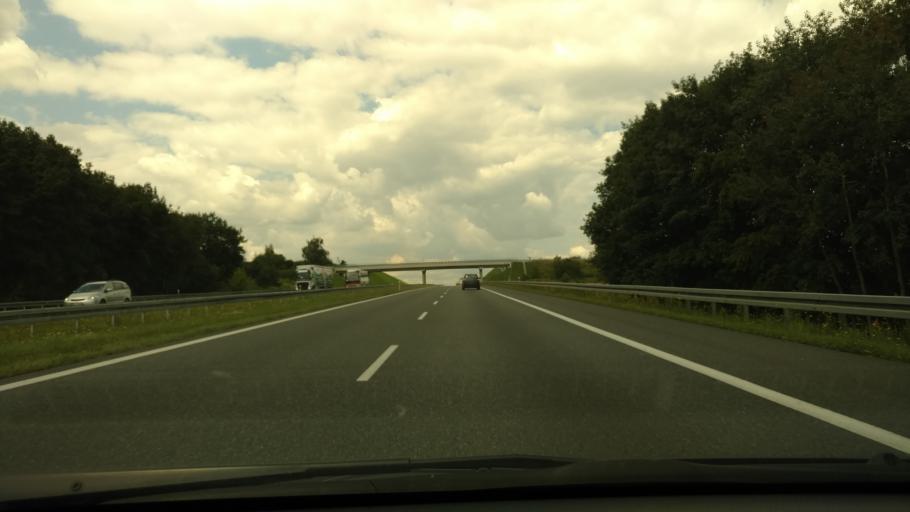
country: PL
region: Silesian Voivodeship
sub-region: Powiat bierunsko-ledzinski
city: Imielin
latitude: 50.1616
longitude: 19.2258
